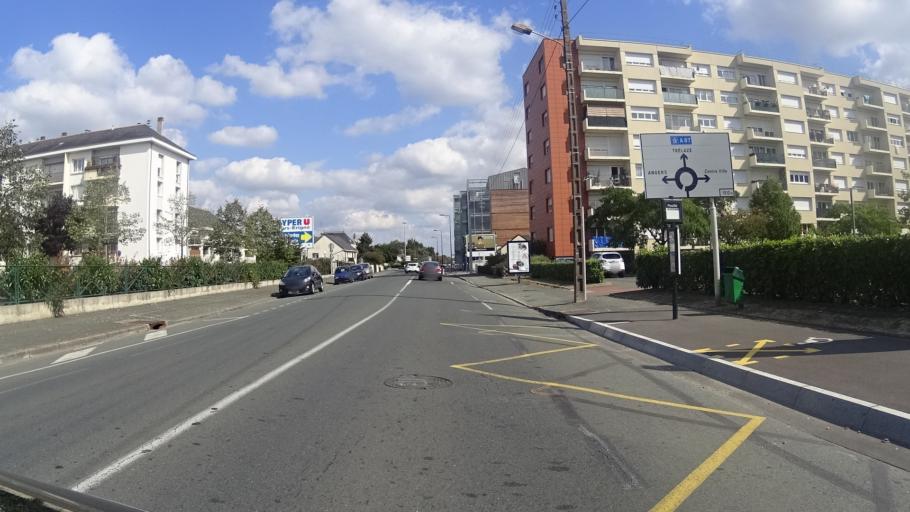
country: FR
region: Pays de la Loire
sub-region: Departement de Maine-et-Loire
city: Les Ponts-de-Ce
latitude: 47.4328
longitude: -0.5319
